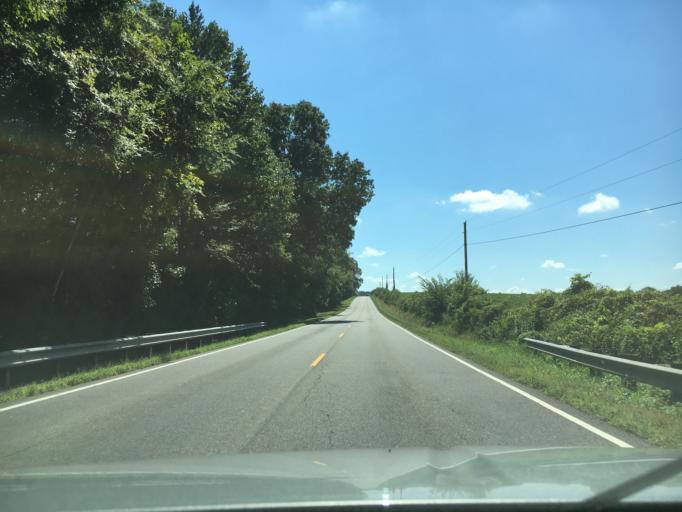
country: US
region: Virginia
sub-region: Amelia County
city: Amelia Court House
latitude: 37.4032
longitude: -77.8961
